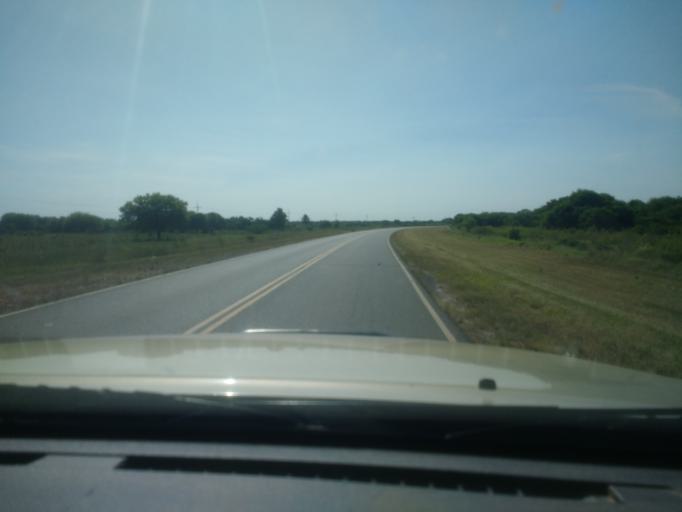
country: PY
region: Presidente Hayes
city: Benjamin Aceval
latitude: -24.9226
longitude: -57.5745
